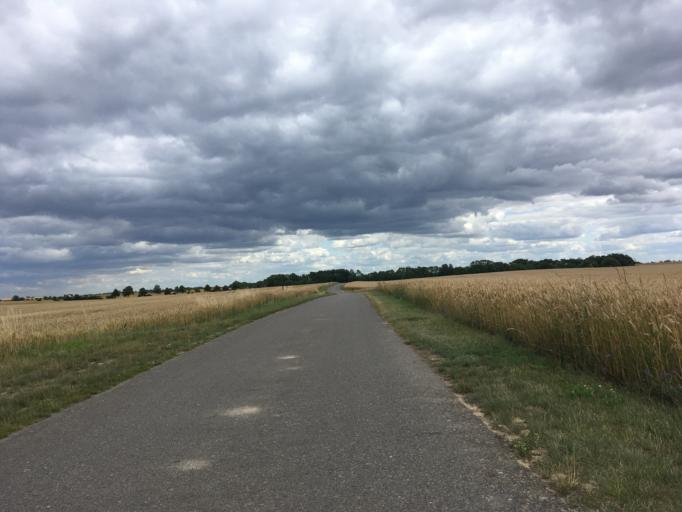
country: DE
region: Brandenburg
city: Gramzow
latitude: 53.2548
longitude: 13.9900
